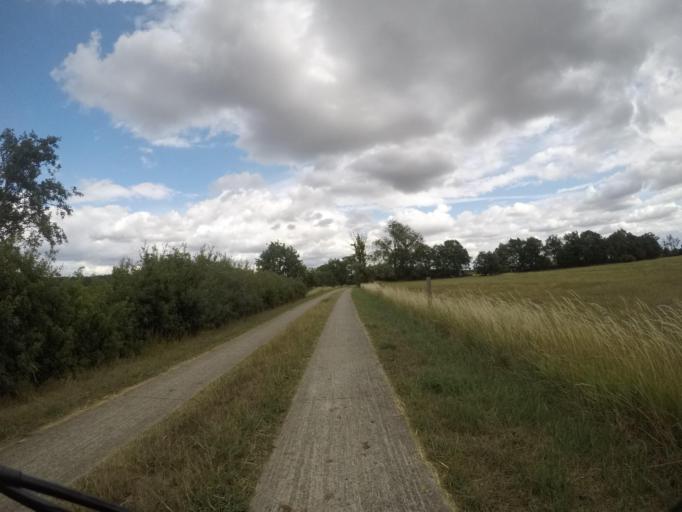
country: DE
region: Lower Saxony
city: Neu Darchau
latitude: 53.2432
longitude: 10.9582
